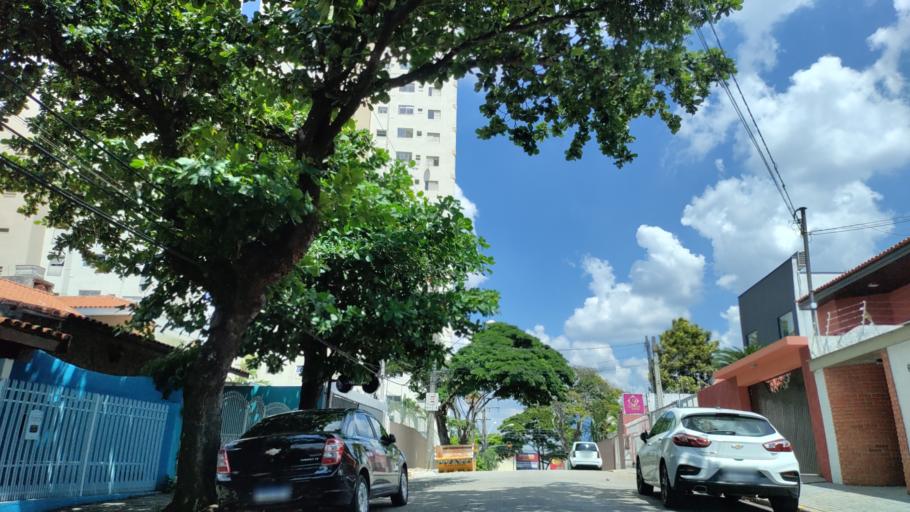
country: BR
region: Sao Paulo
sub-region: Sorocaba
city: Sorocaba
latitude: -23.4917
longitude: -47.4686
